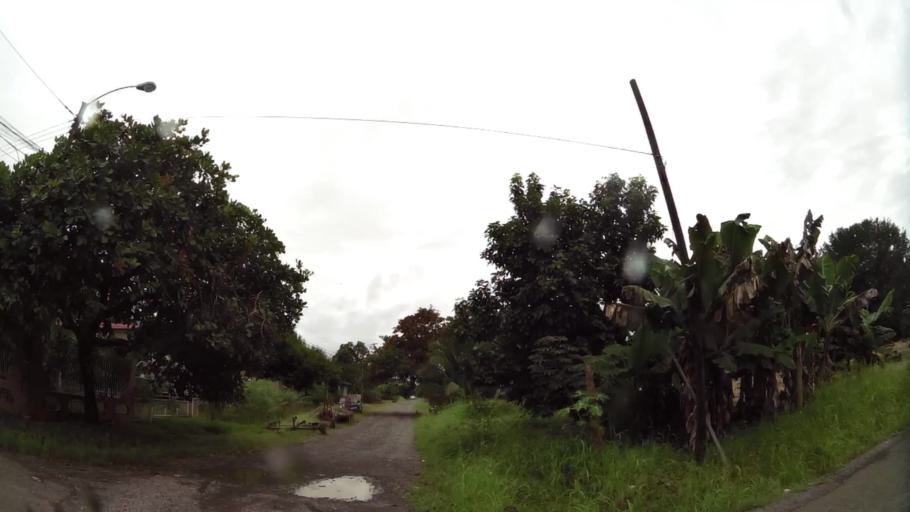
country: PA
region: Chiriqui
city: David
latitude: 8.4013
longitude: -82.4556
